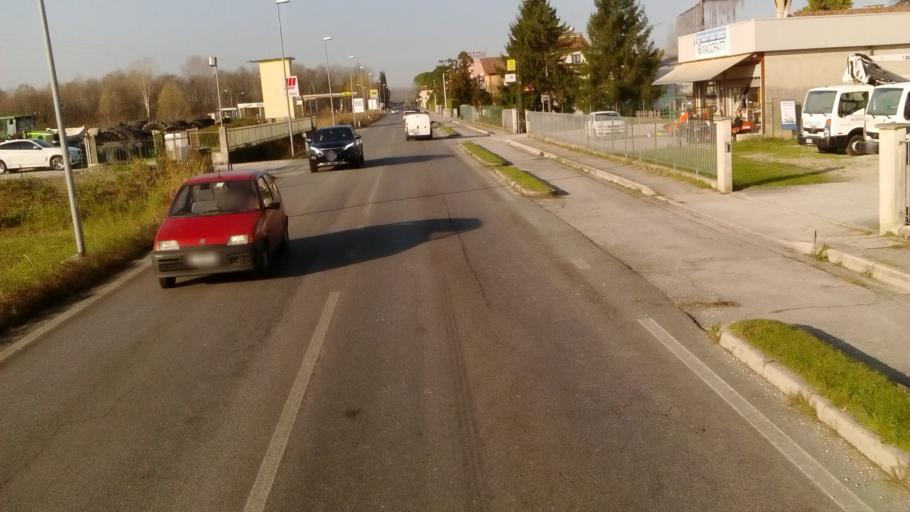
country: IT
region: Friuli Venezia Giulia
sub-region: Provincia di Udine
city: San Giorgio di Nogaro
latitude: 45.8340
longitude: 13.1975
